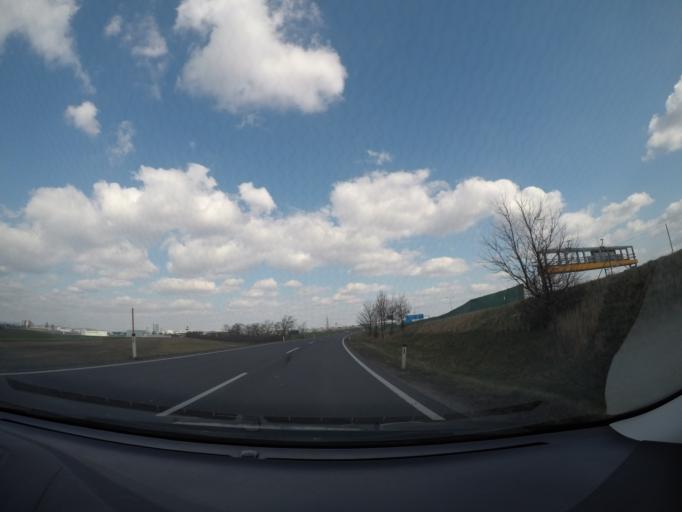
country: AT
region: Lower Austria
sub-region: Politischer Bezirk Modling
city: Vosendorf
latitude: 48.1302
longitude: 16.3328
